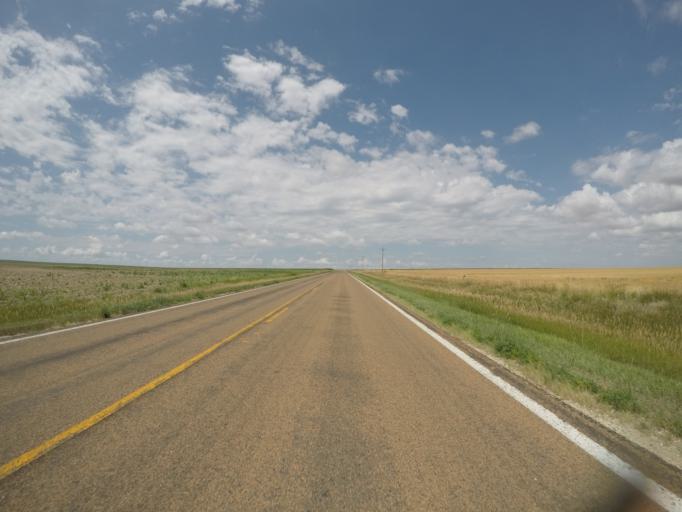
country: US
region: Kansas
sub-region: Rawlins County
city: Atwood
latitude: 39.9558
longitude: -101.0561
